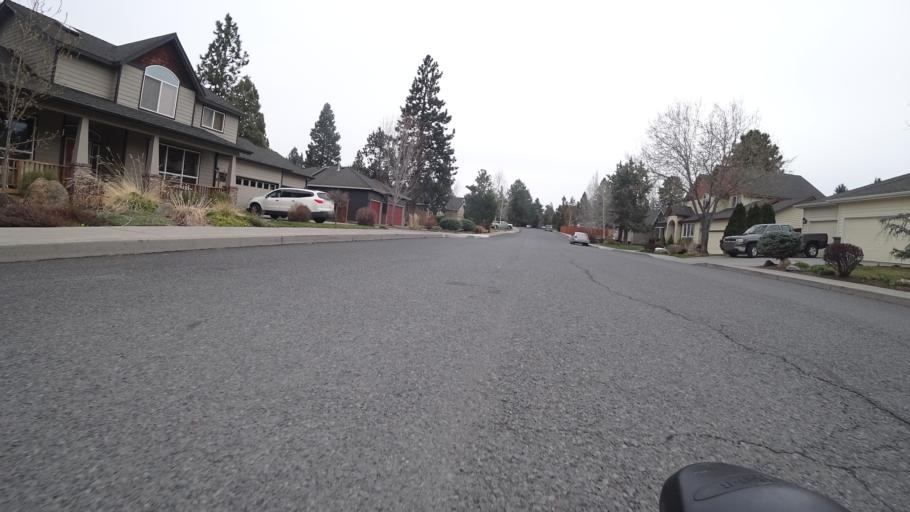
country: US
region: Oregon
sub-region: Deschutes County
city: Bend
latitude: 44.0406
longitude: -121.2753
